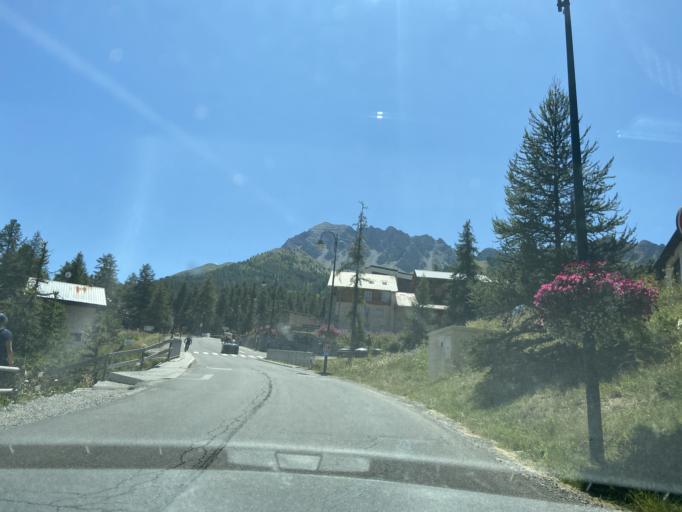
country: FR
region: Provence-Alpes-Cote d'Azur
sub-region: Departement des Hautes-Alpes
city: Guillestre
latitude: 44.5751
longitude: 6.6818
